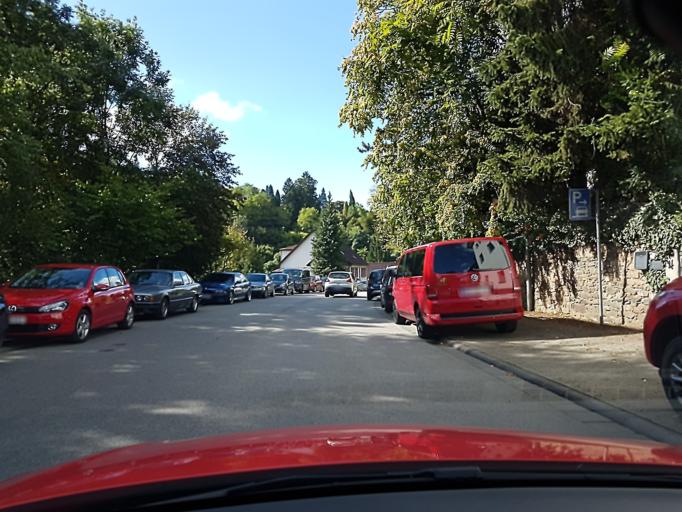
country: DE
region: Hesse
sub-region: Regierungsbezirk Darmstadt
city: Bensheim
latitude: 49.7034
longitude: 8.6299
